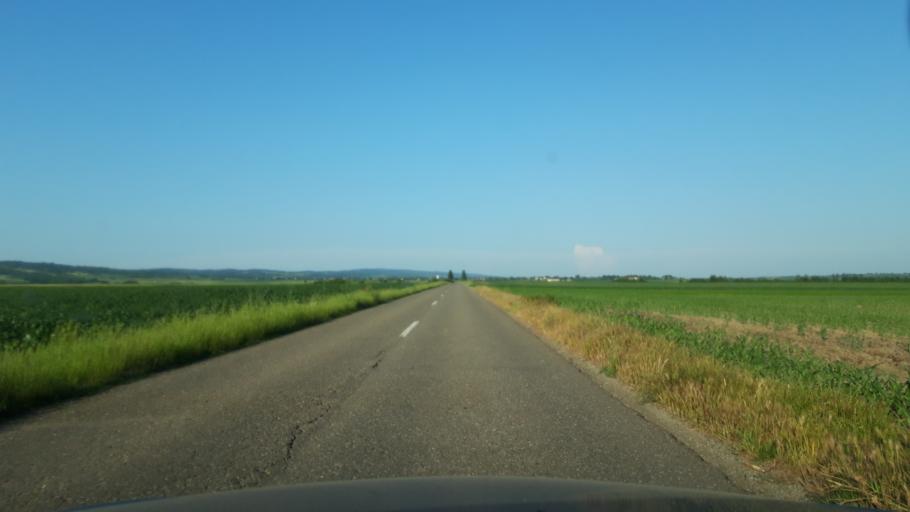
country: HR
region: Vukovarsko-Srijemska
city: Ilok
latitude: 45.1031
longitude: 19.4682
